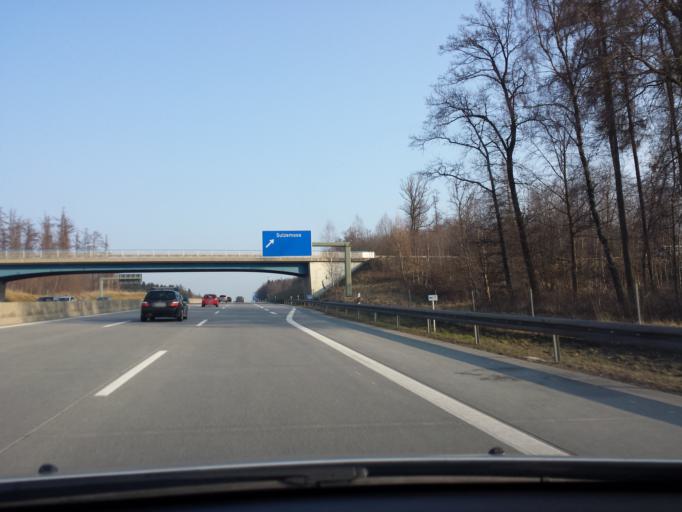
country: DE
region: Bavaria
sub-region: Upper Bavaria
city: Sulzemoos
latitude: 48.2813
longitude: 11.2692
